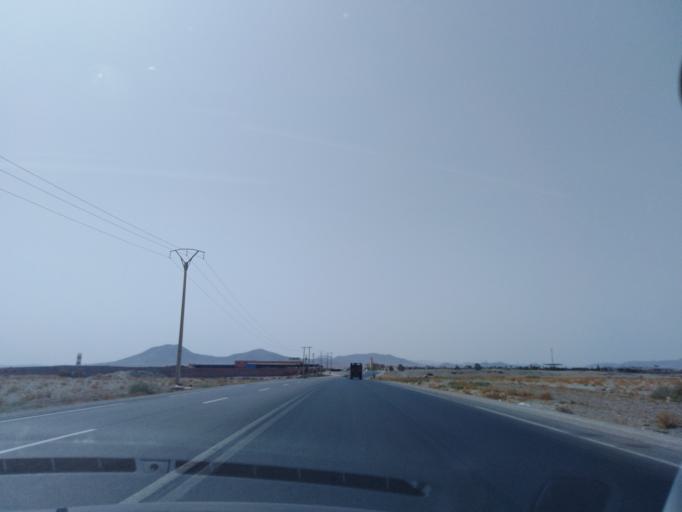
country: MA
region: Marrakech-Tensift-Al Haouz
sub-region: Marrakech
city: Marrakesh
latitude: 31.7693
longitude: -8.1250
